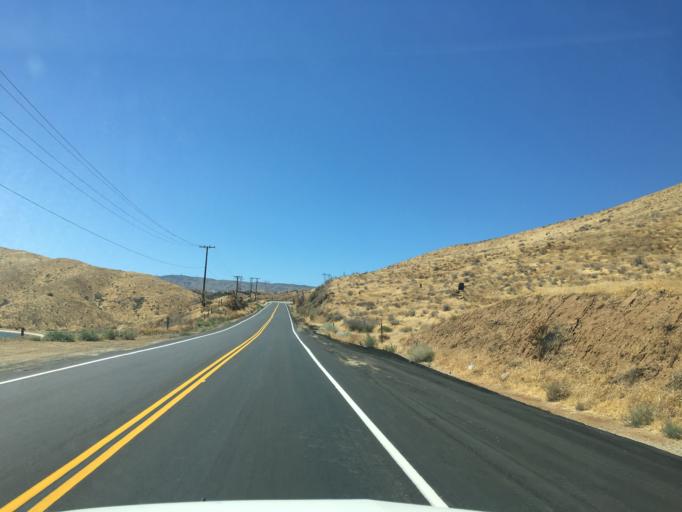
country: US
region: California
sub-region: Los Angeles County
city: Quartz Hill
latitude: 34.6190
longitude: -118.2335
